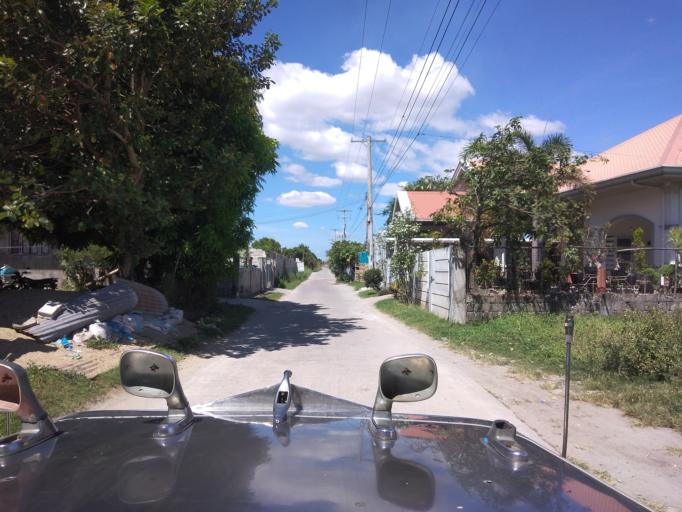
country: PH
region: Central Luzon
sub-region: Province of Pampanga
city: Magliman
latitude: 15.0507
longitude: 120.6417
